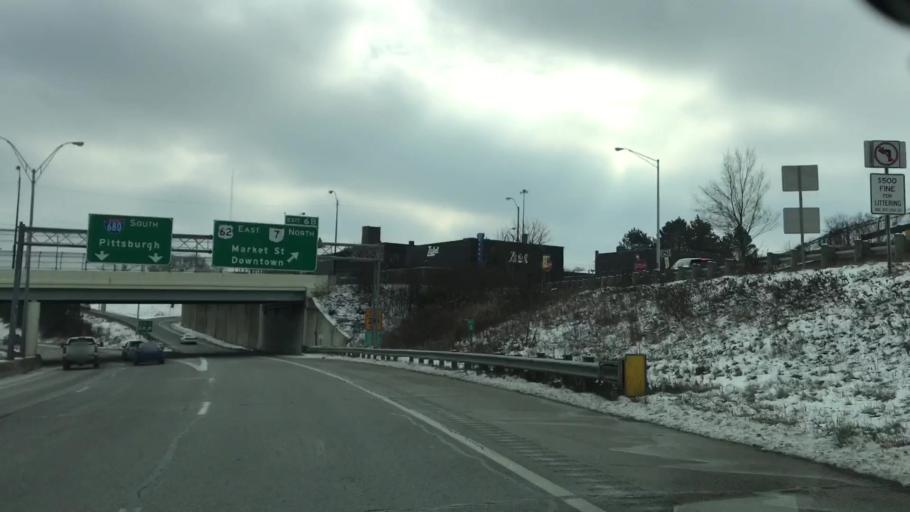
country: US
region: Ohio
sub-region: Mahoning County
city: Youngstown
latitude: 41.0931
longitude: -80.6557
